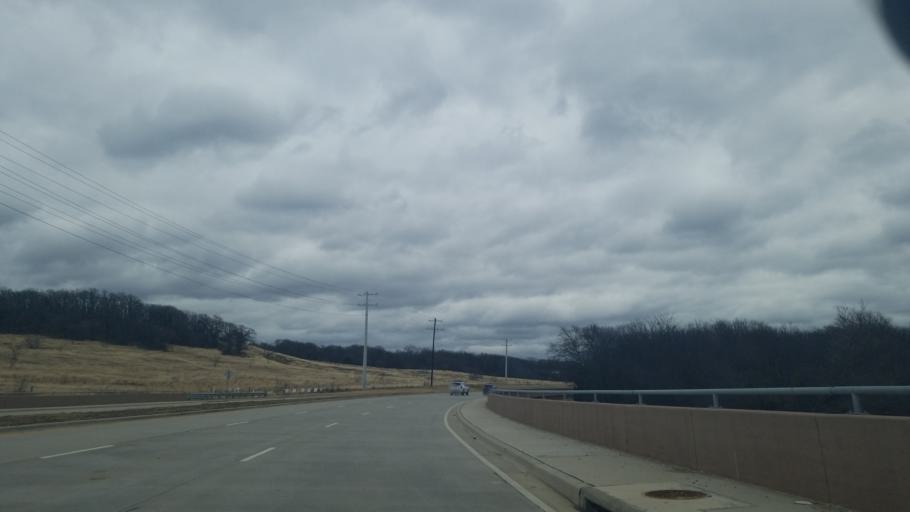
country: US
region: Texas
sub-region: Denton County
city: Trophy Club
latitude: 33.0508
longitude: -97.1817
